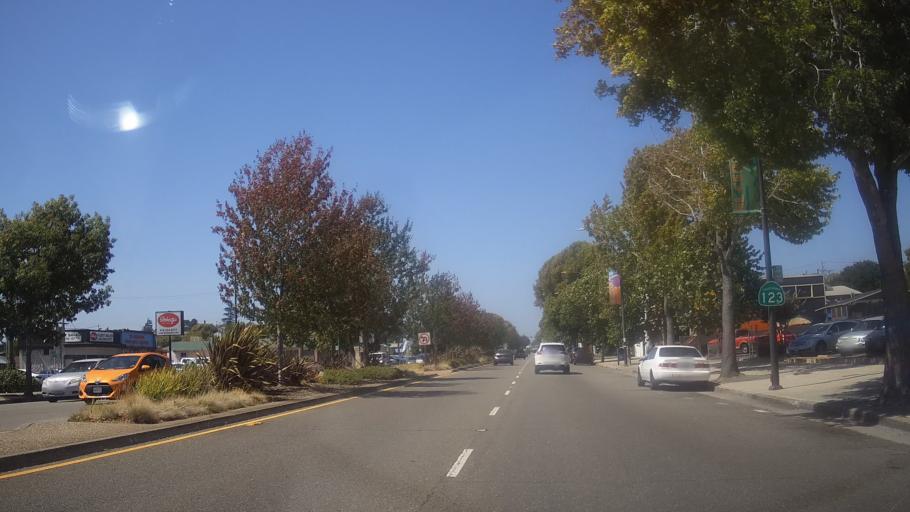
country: US
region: California
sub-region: Contra Costa County
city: El Cerrito
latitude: 37.9081
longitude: -122.3065
